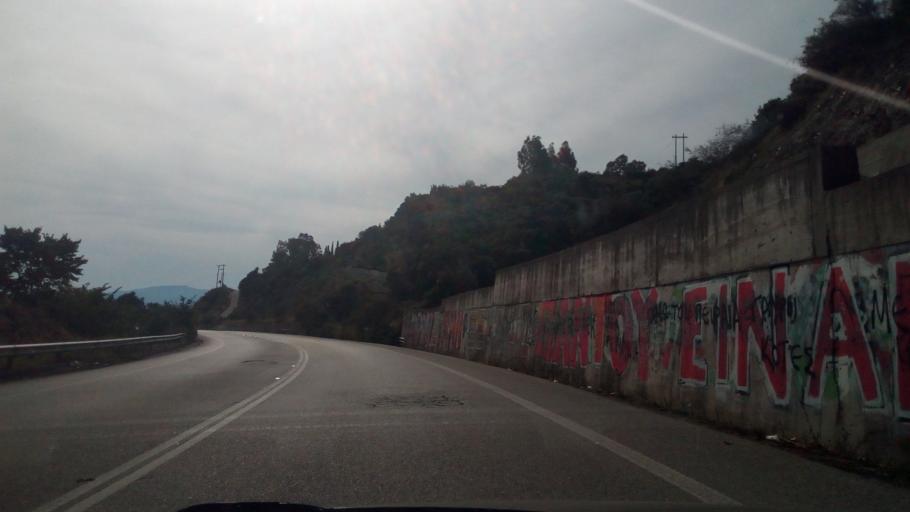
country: GR
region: West Greece
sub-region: Nomos Aitolias kai Akarnanias
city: Nafpaktos
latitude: 38.3940
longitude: 21.7928
